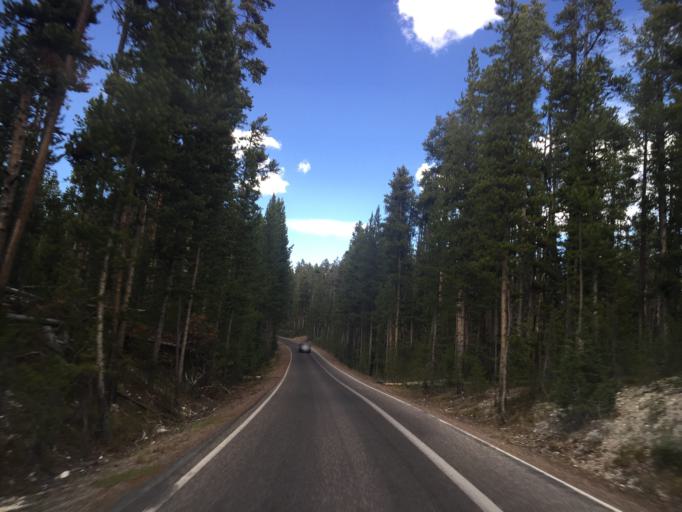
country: US
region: Montana
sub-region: Gallatin County
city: West Yellowstone
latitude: 44.7307
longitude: -110.4812
